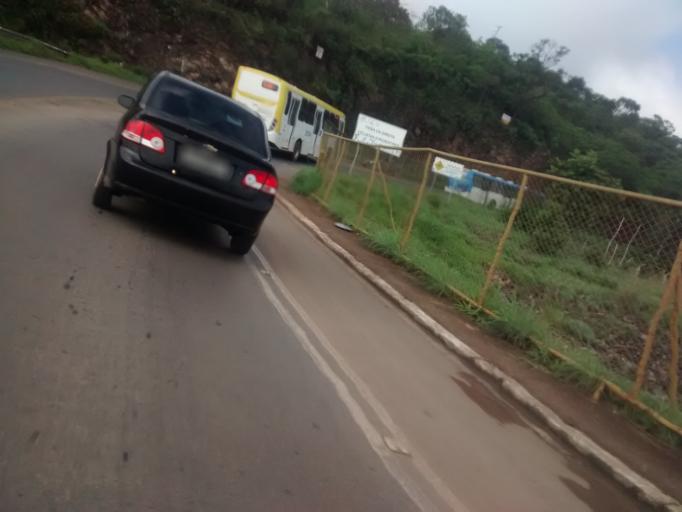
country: BR
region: Federal District
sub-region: Brasilia
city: Brasilia
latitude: -15.8021
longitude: -47.7858
